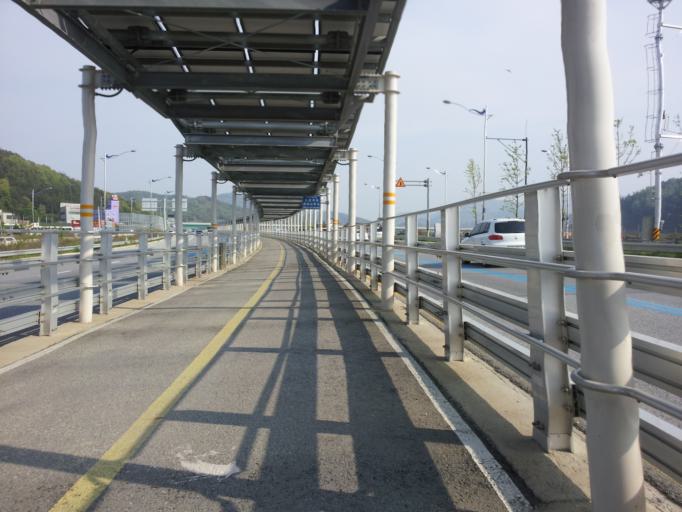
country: KR
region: Daejeon
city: Songgang-dong
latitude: 36.4635
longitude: 127.2760
